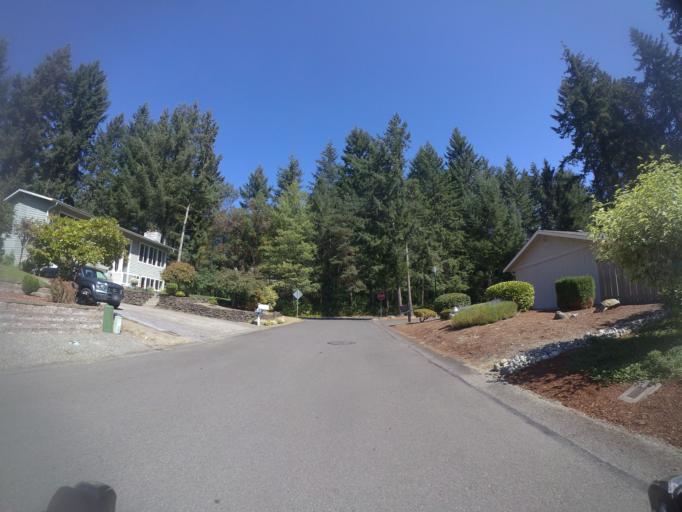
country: US
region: Washington
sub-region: Pierce County
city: University Place
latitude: 47.2165
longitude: -122.5621
